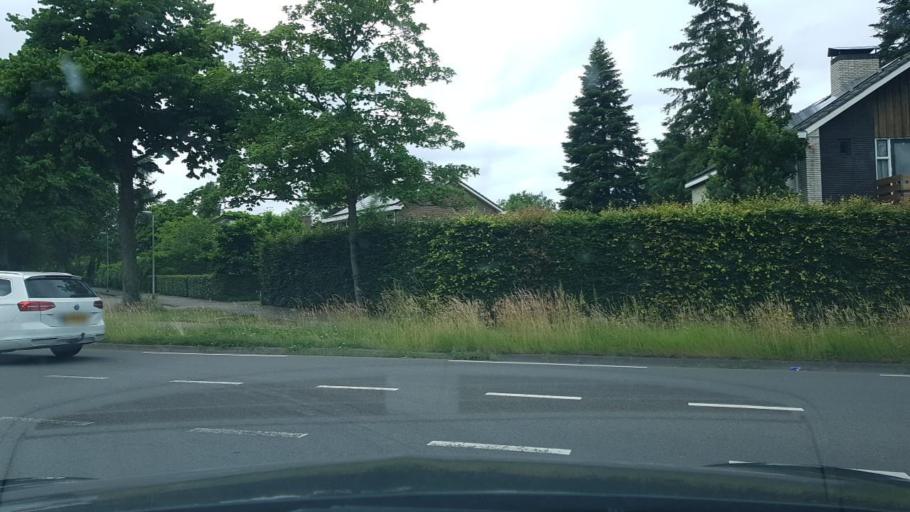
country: NL
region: Overijssel
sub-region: Gemeente Deventer
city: Deventer
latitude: 52.2648
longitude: 6.1766
